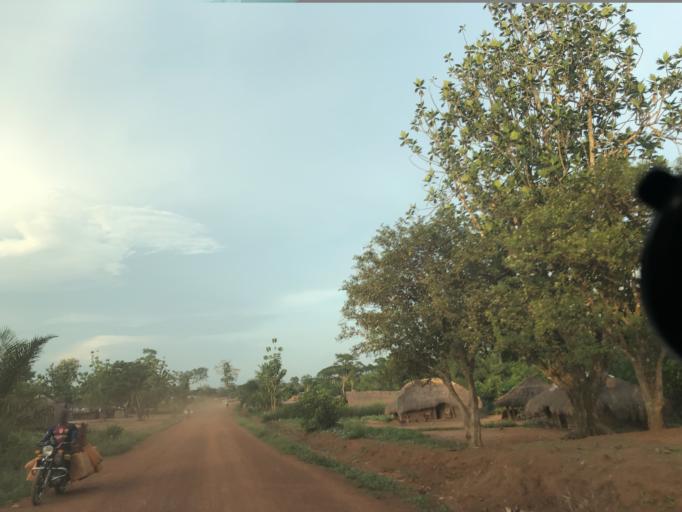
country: CF
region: Bangui
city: Bangui
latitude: 4.1489
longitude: 18.7829
